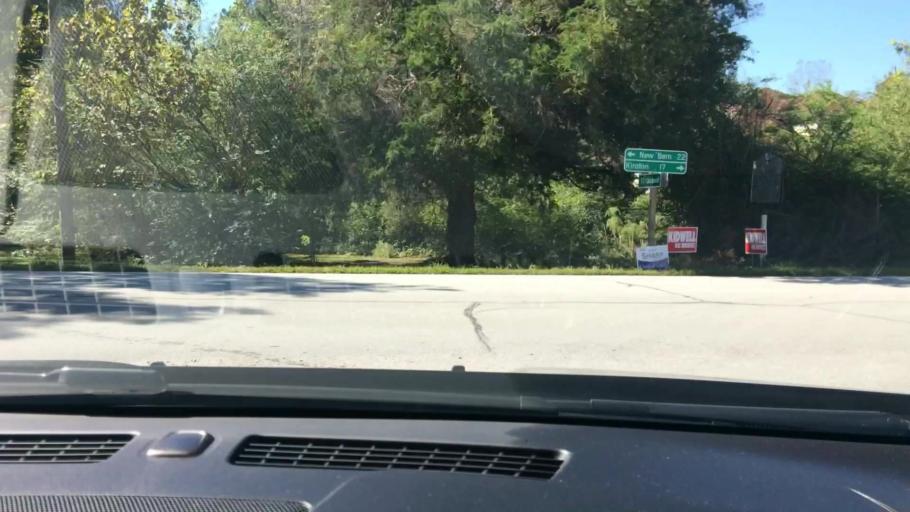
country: US
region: North Carolina
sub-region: Pitt County
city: Grifton
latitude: 35.2921
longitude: -77.3358
